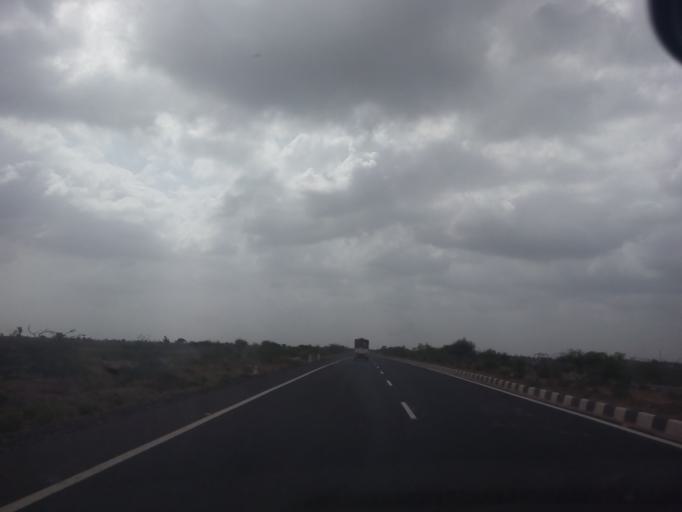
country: IN
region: Gujarat
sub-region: Surendranagar
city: Halvad
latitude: 23.0258
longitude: 70.9724
